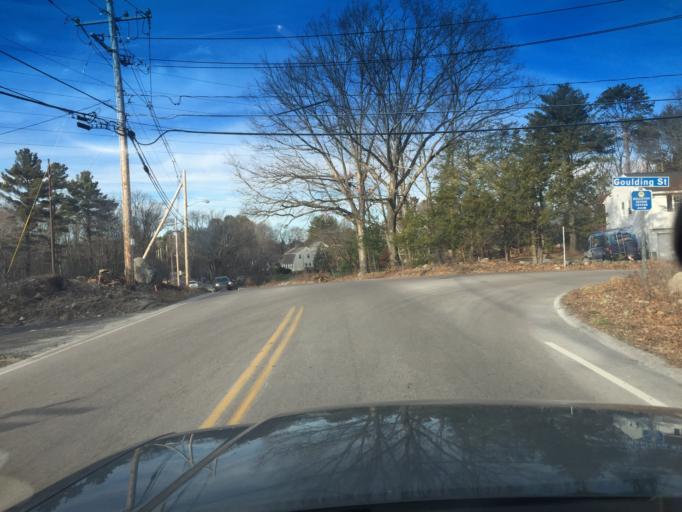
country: US
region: Massachusetts
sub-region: Middlesex County
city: Holliston
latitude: 42.1816
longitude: -71.4115
